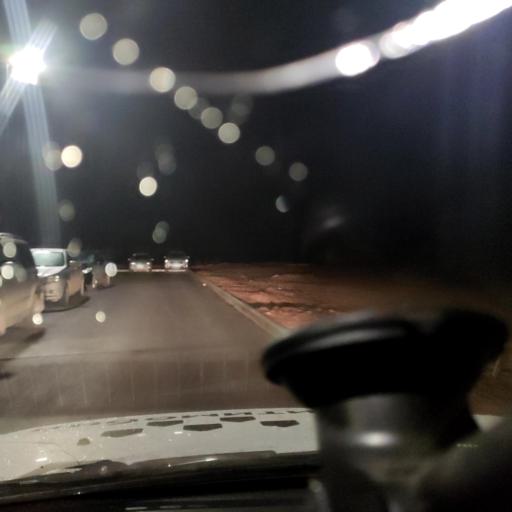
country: RU
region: Perm
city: Perm
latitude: 58.0083
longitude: 56.3340
